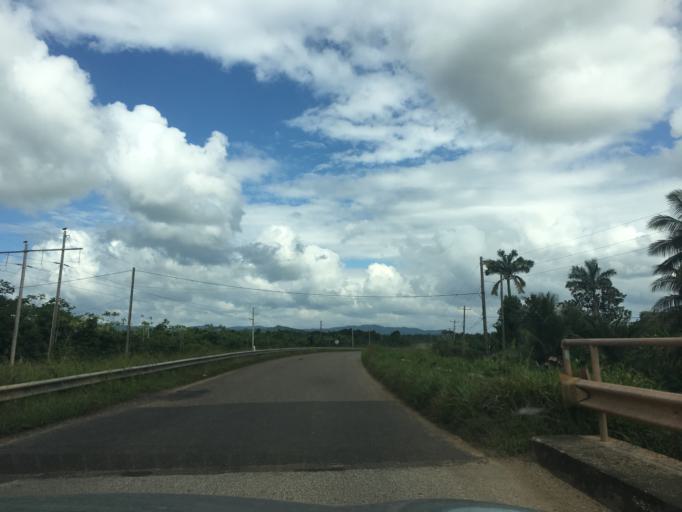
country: BZ
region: Stann Creek
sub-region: Dangriga
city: Dangriga
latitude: 16.8624
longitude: -88.3473
